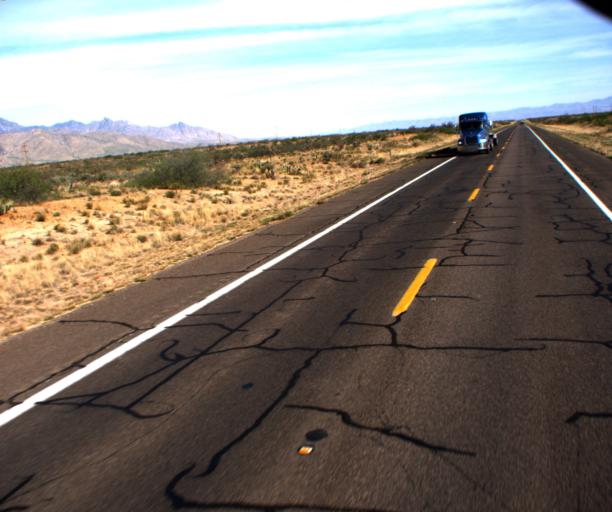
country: US
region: Arizona
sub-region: Graham County
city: Swift Trail Junction
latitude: 32.6090
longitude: -109.6871
